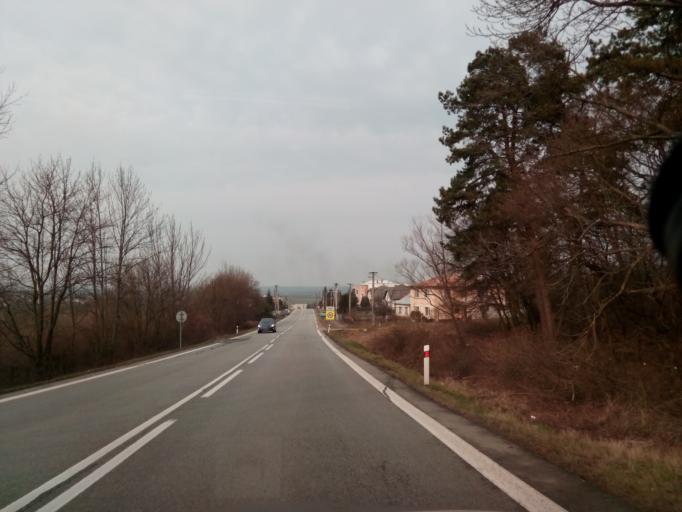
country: HU
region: Borsod-Abauj-Zemplen
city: Satoraljaujhely
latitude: 48.5170
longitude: 21.6592
